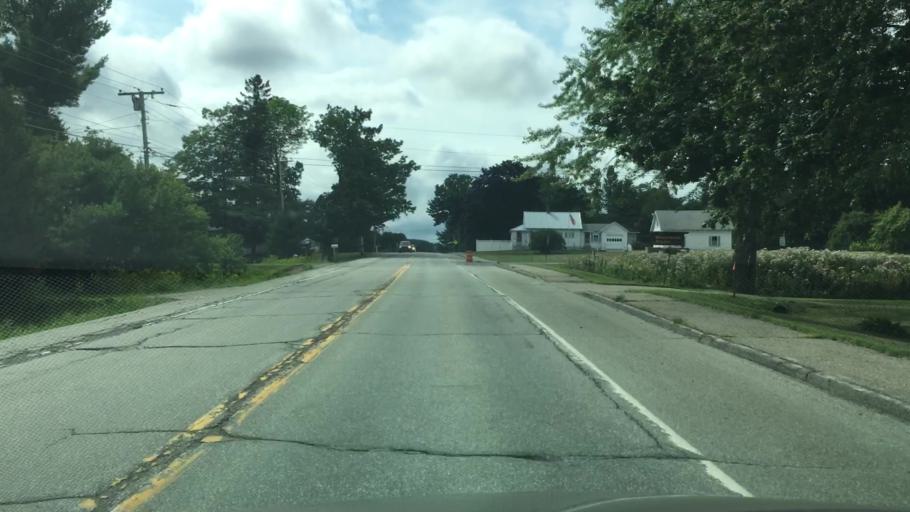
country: US
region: Maine
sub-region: Penobscot County
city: Hampden
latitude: 44.7459
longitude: -68.8541
